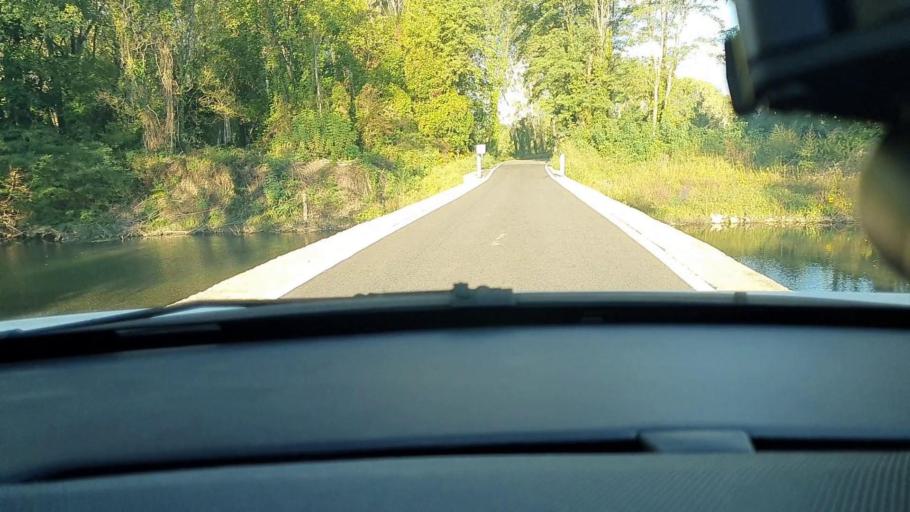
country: FR
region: Languedoc-Roussillon
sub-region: Departement du Gard
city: Saint-Ambroix
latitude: 44.2350
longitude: 4.2735
